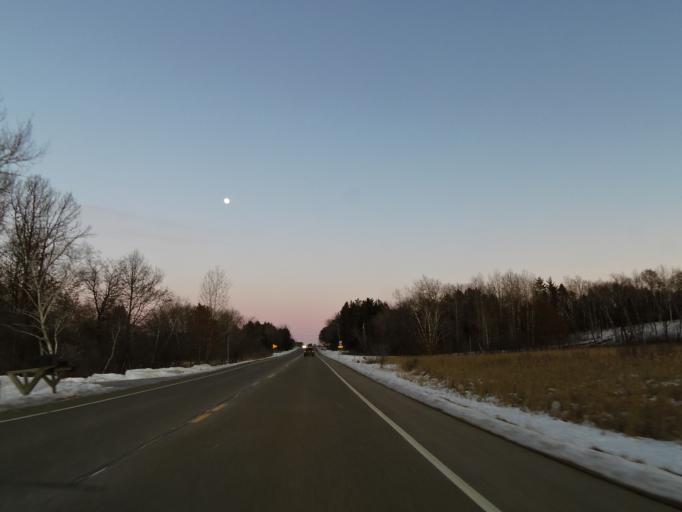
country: US
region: Minnesota
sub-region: Washington County
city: Grant
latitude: 45.0795
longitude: -92.8706
